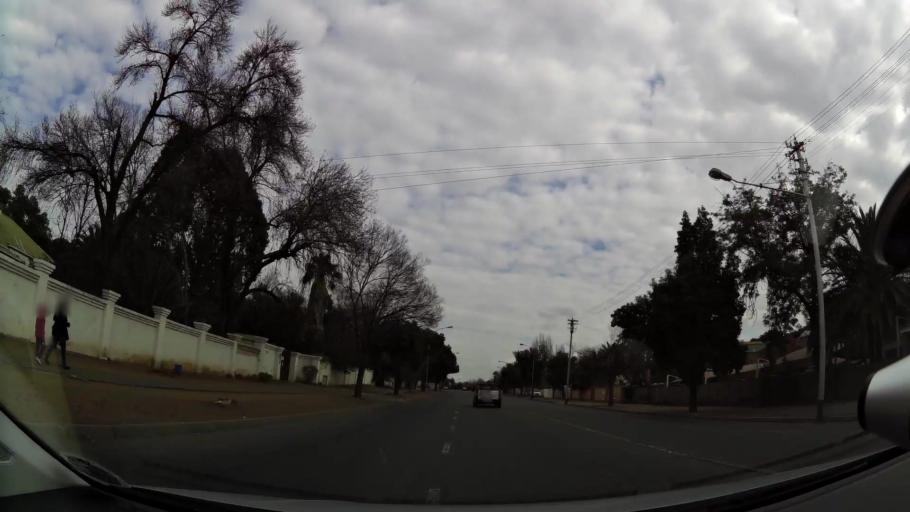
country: ZA
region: Orange Free State
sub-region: Mangaung Metropolitan Municipality
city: Bloemfontein
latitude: -29.0968
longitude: 26.2248
